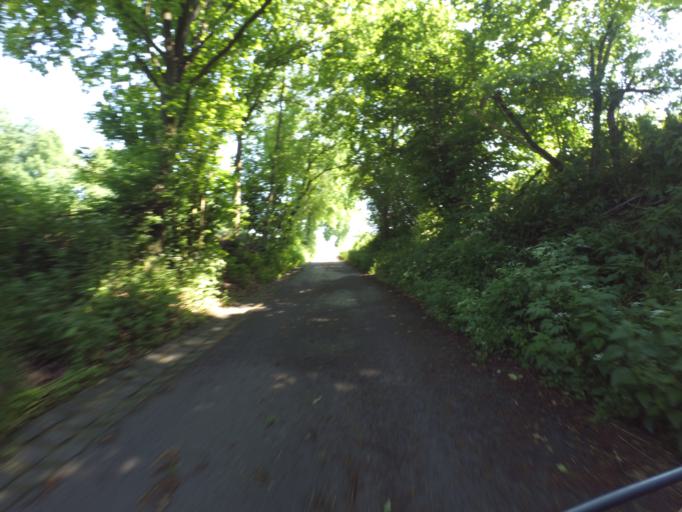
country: DE
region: Rheinland-Pfalz
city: Roes
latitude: 50.2558
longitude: 7.2687
